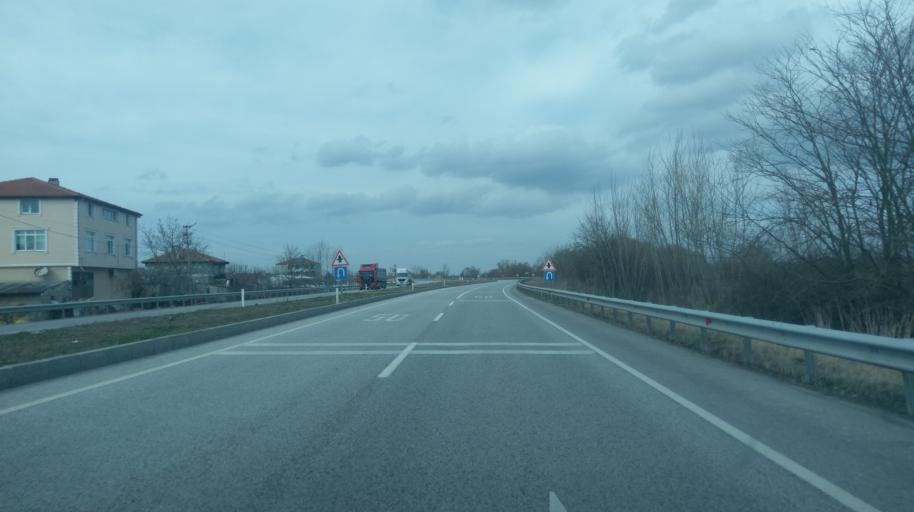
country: TR
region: Edirne
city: Kircasalih
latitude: 41.4663
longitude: 26.8220
